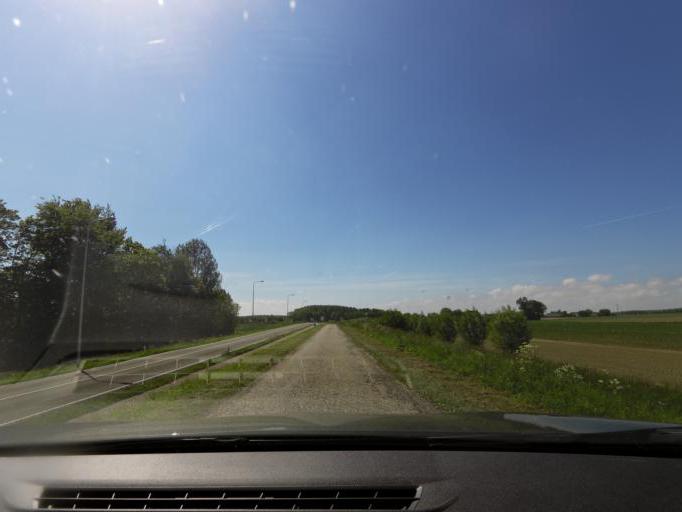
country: NL
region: South Holland
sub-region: Gemeente Goeree-Overflakkee
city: Dirksland
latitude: 51.7681
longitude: 4.0886
